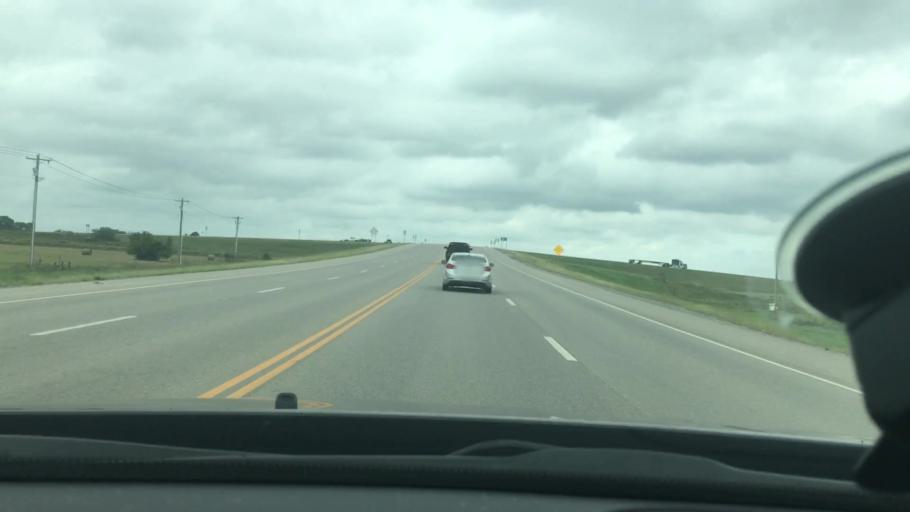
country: US
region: Oklahoma
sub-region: Bryan County
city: Durant
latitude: 33.9615
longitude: -96.3732
